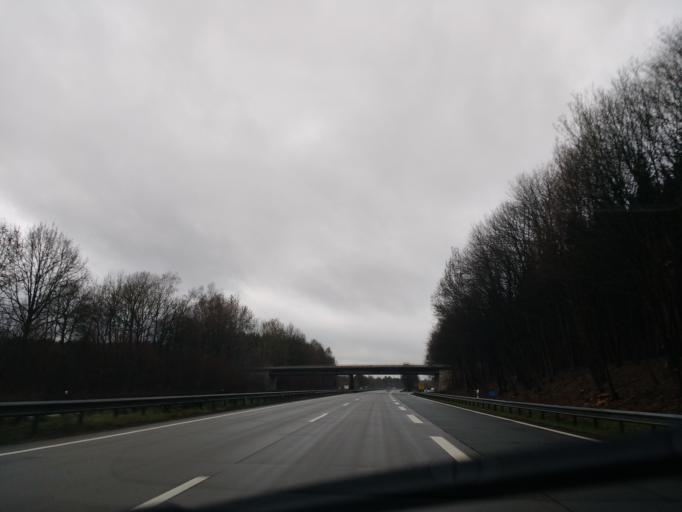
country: DE
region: Lower Saxony
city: Langen
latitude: 53.6121
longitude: 8.6611
